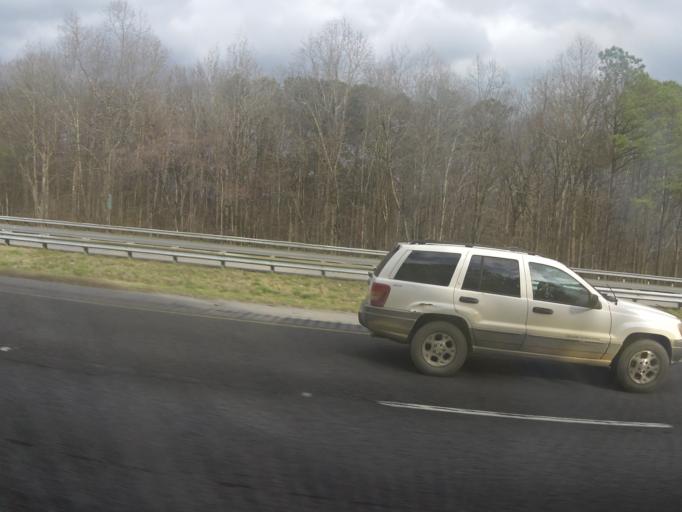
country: US
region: Georgia
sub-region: Whitfield County
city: Dalton
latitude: 34.7109
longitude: -85.0074
